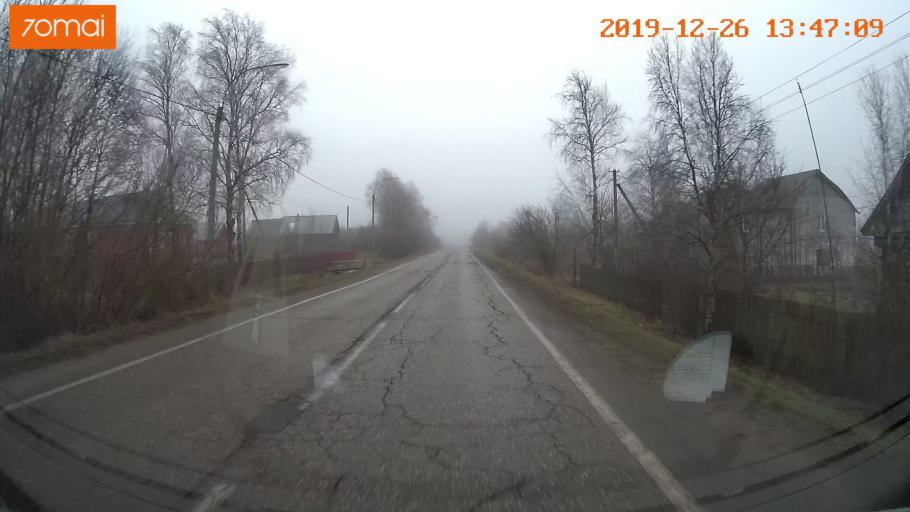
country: RU
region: Vologda
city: Sheksna
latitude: 58.6869
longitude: 38.5314
